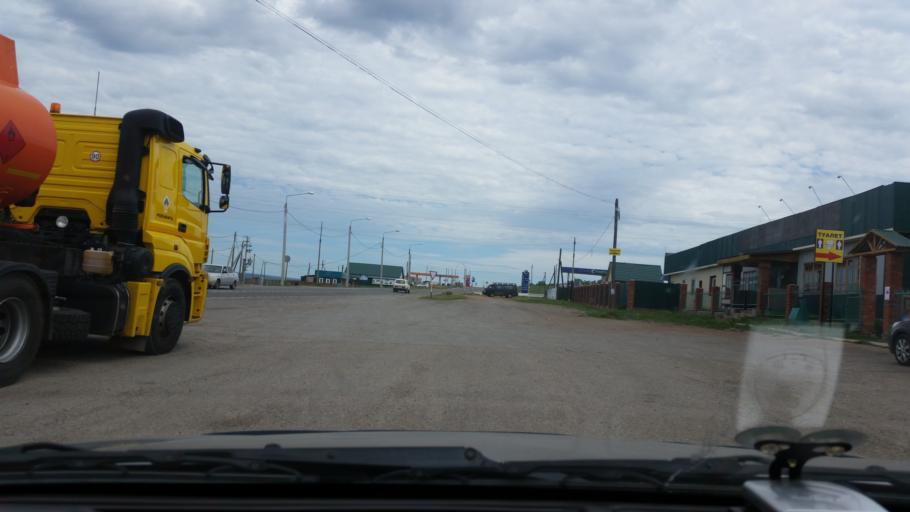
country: RU
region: Irkutsk
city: Bayanday
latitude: 53.0413
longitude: 105.5104
